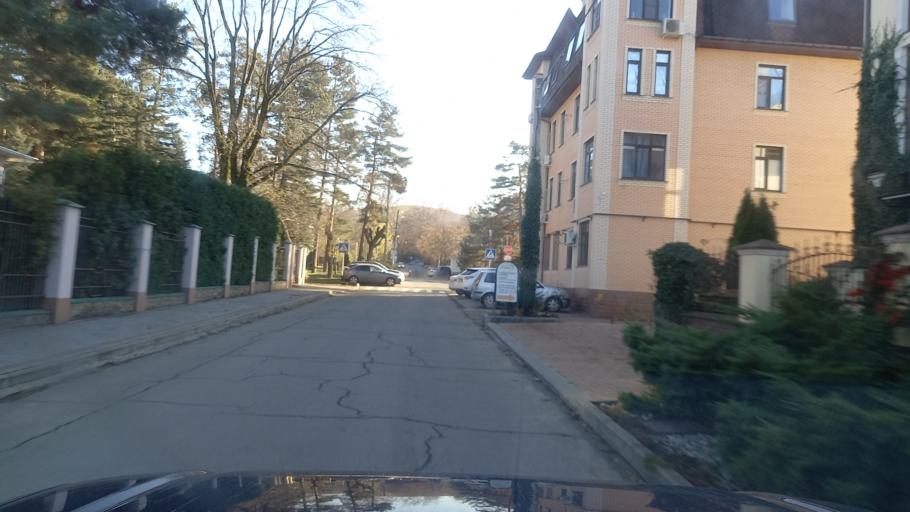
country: RU
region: Krasnodarskiy
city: Goryachiy Klyuch
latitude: 44.6273
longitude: 39.1051
